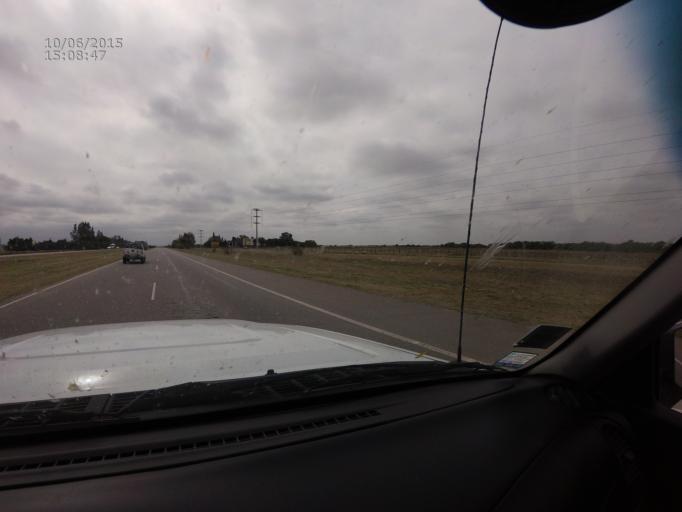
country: AR
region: Cordoba
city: Pilar
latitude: -31.6456
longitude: -63.8614
